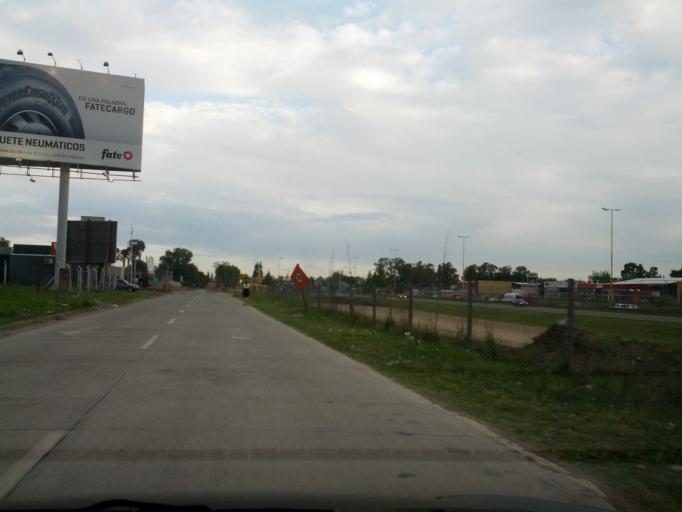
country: AR
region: Buenos Aires
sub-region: Partido de General Rodriguez
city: General Rodriguez
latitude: -34.6146
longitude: -58.8527
